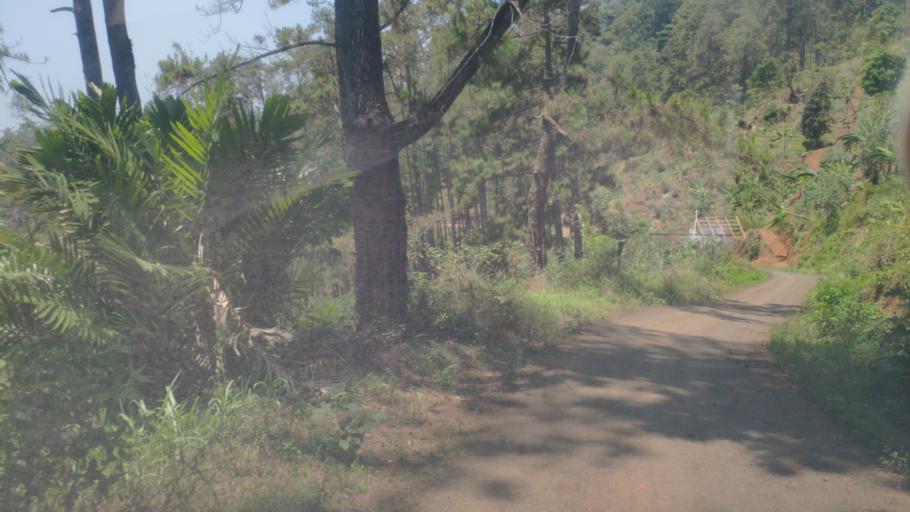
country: ID
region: Central Java
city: Buaran
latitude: -7.2825
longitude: 109.5902
